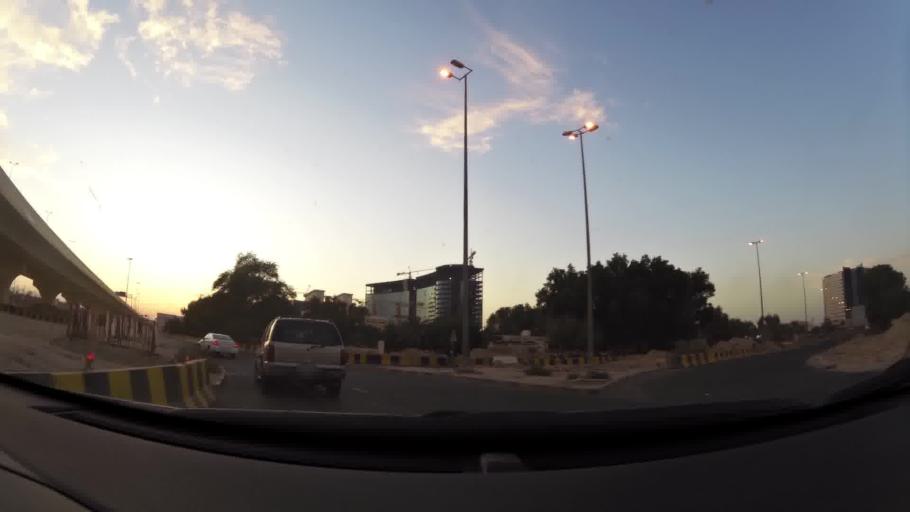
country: KW
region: Al Asimah
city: Ar Rabiyah
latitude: 29.3326
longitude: 47.9086
